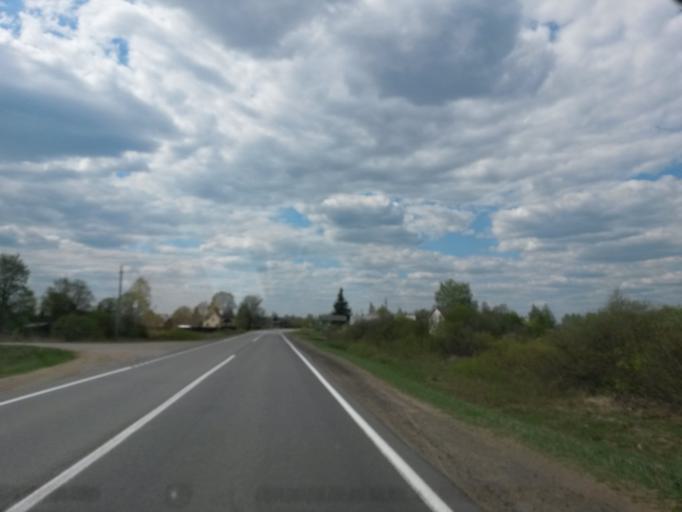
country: RU
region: Jaroslavl
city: Konstantinovskiy
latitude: 57.6687
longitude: 39.6435
